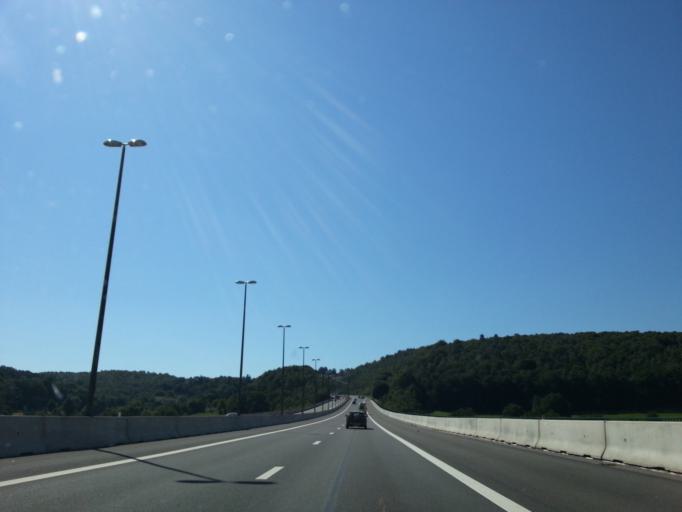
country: BE
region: Wallonia
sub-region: Province de Liege
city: Spa
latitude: 50.5355
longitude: 5.8756
